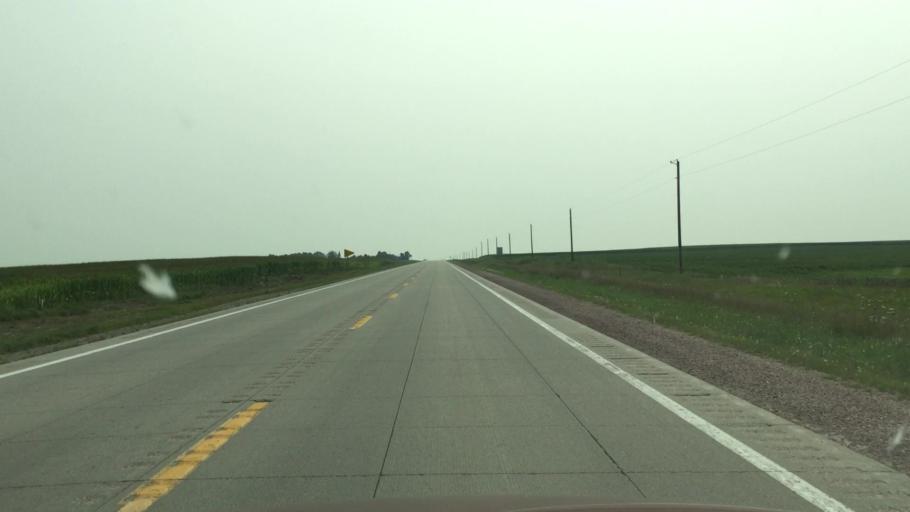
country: US
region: Iowa
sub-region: Osceola County
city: Sibley
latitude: 43.4328
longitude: -95.6384
